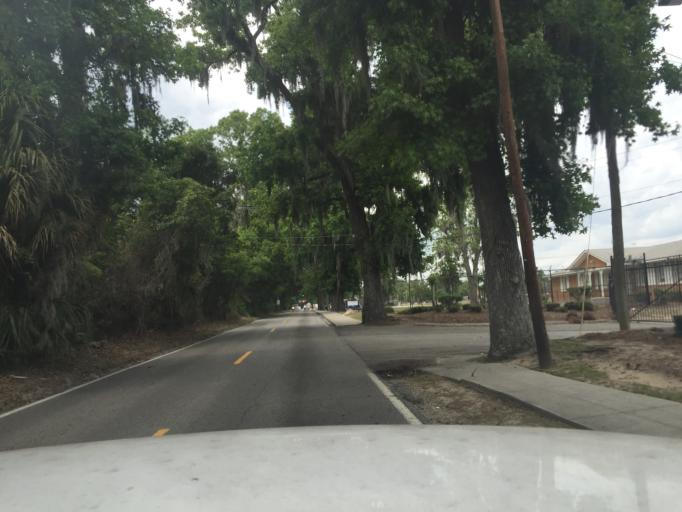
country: US
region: Georgia
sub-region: Chatham County
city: Thunderbolt
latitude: 32.0241
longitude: -81.0693
